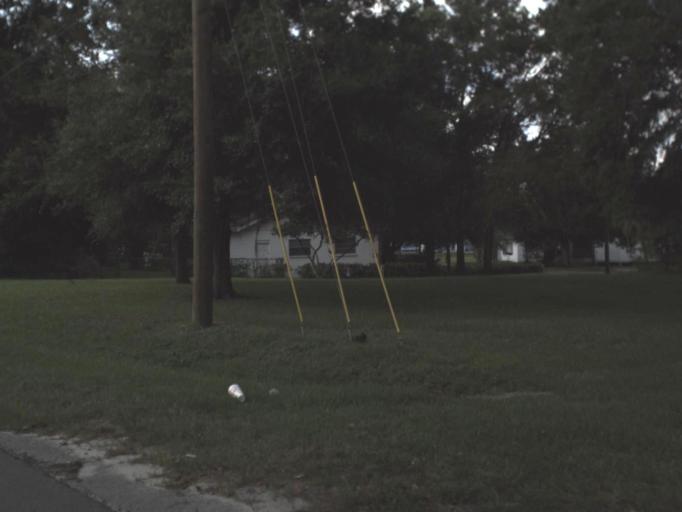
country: US
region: Florida
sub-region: Pasco County
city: Dade City
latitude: 28.3711
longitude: -82.1872
